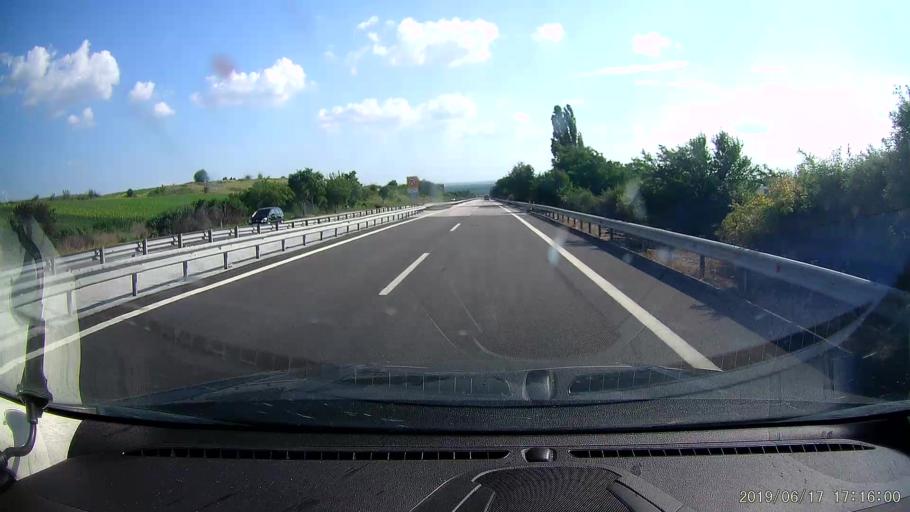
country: GR
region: East Macedonia and Thrace
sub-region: Nomos Evrou
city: Kastanies
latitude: 41.6979
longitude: 26.4865
